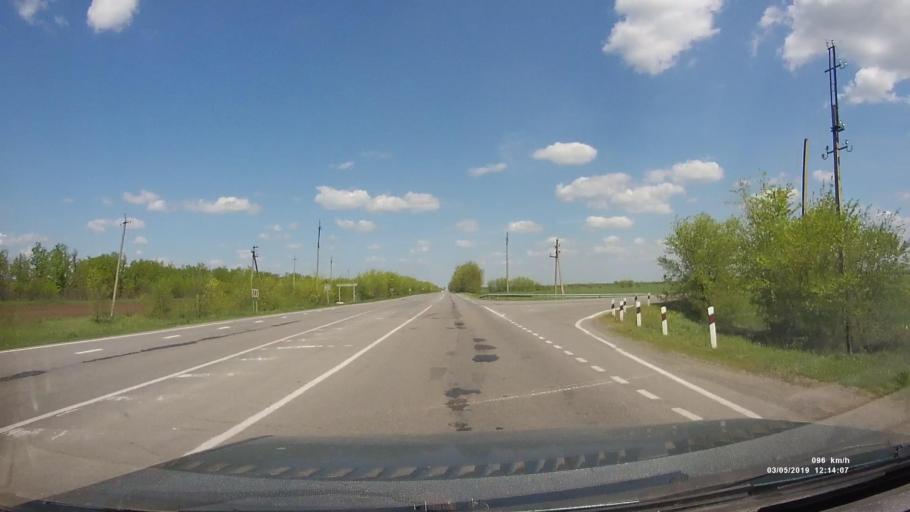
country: RU
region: Rostov
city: Melikhovskaya
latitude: 47.3397
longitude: 40.5602
